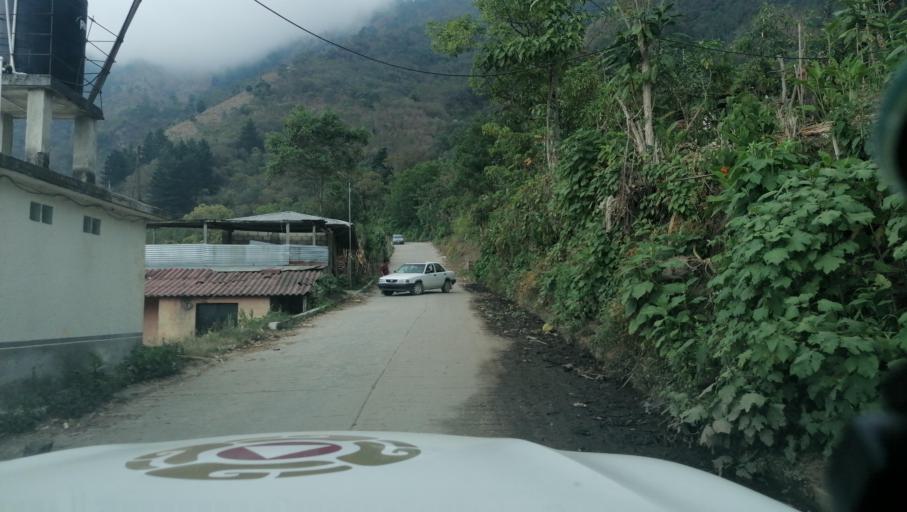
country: GT
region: San Marcos
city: Tacana
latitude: 15.2031
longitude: -92.1810
